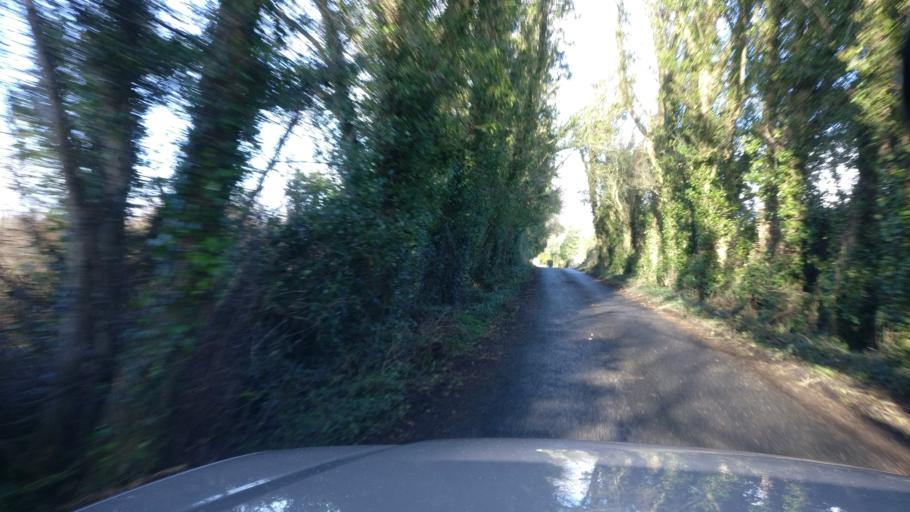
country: IE
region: Connaught
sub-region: County Galway
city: Athenry
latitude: 53.2228
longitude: -8.6695
